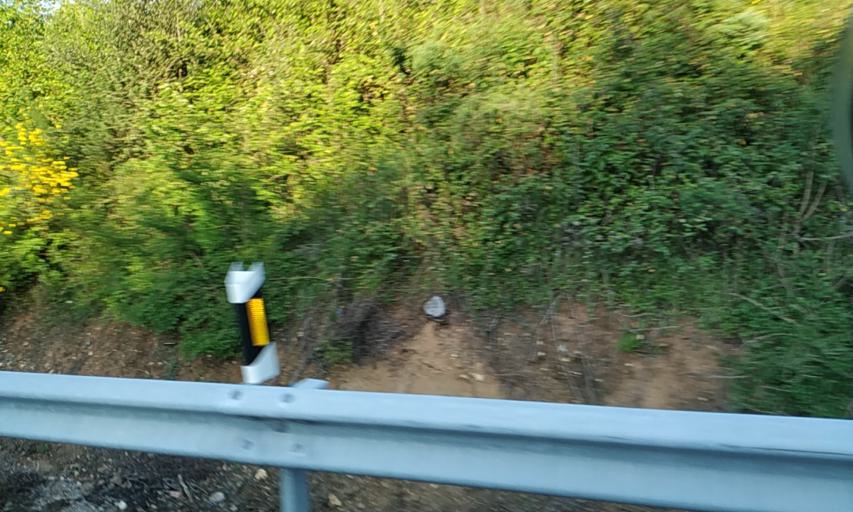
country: PT
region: Portalegre
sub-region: Portalegre
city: Sao Juliao
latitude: 39.3471
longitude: -7.2756
